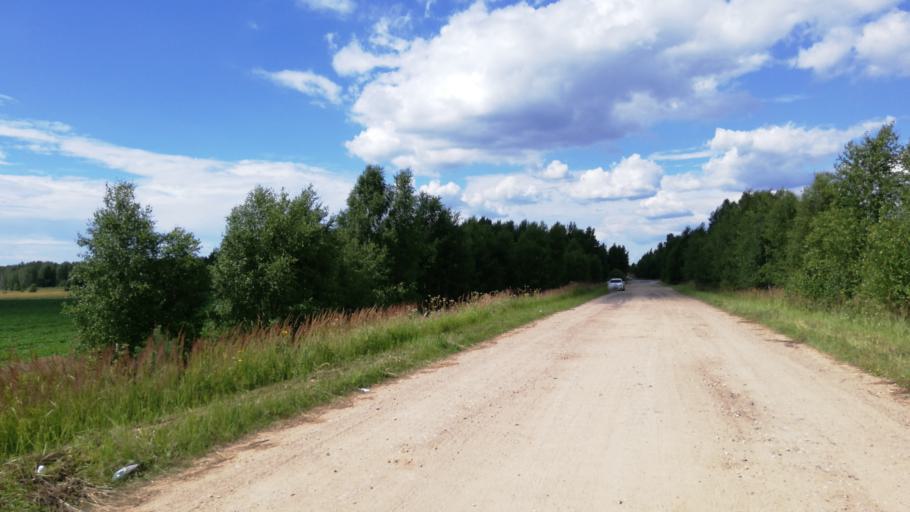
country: RU
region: Jaroslavl
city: Levashevo
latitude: 57.6371
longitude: 40.4632
